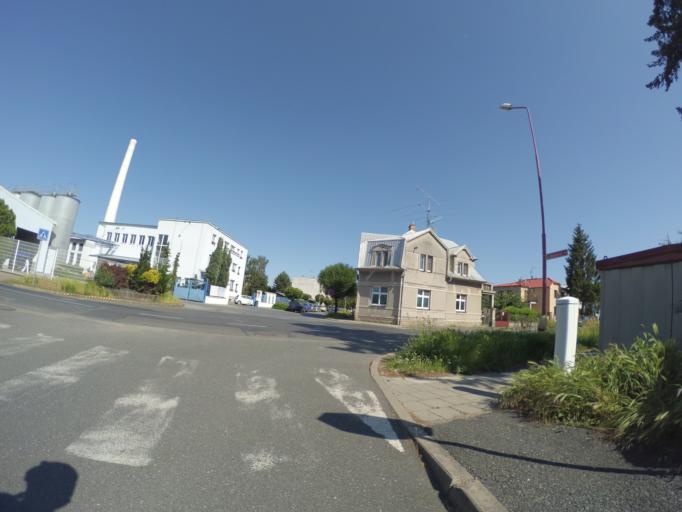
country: CZ
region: Central Bohemia
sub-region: Okres Nymburk
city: Podebrady
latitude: 50.1531
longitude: 15.1094
